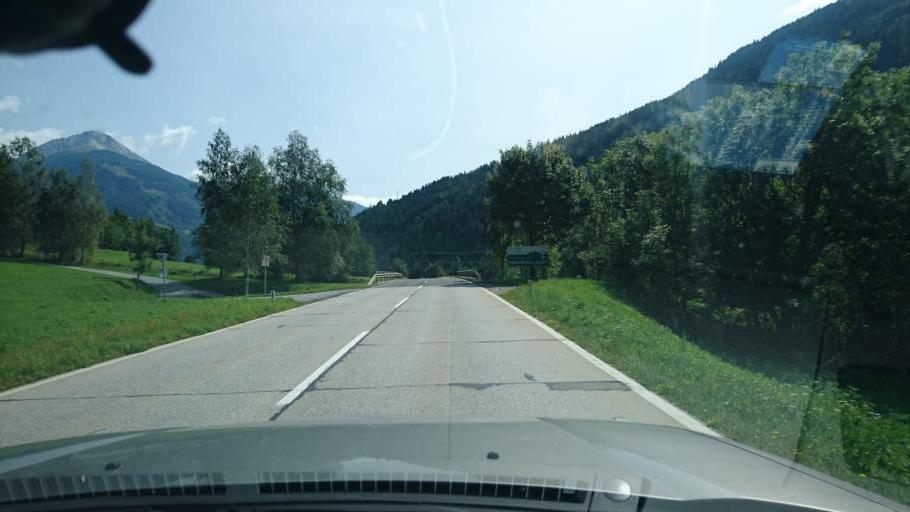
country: AT
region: Carinthia
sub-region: Politischer Bezirk Spittal an der Drau
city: Flattach
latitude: 46.9348
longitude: 13.1603
